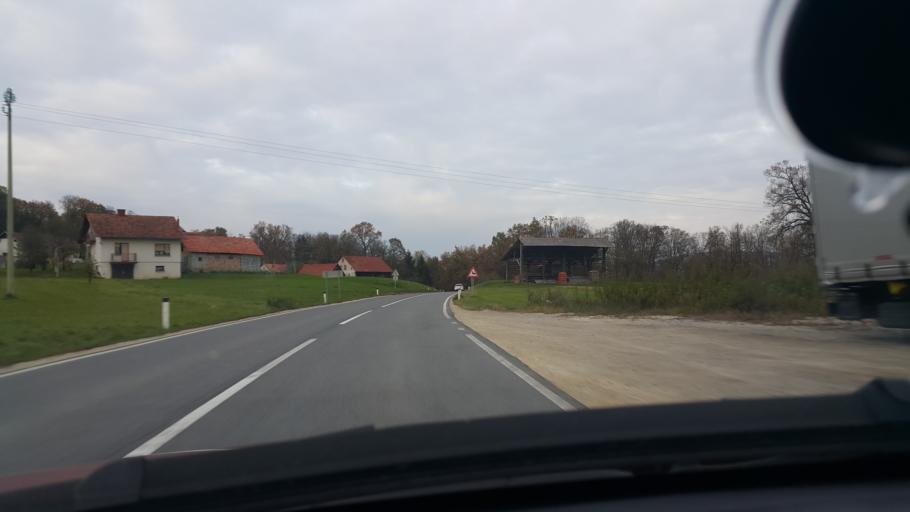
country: SI
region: Podcetrtek
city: Podcetrtek
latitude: 46.1108
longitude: 15.6022
